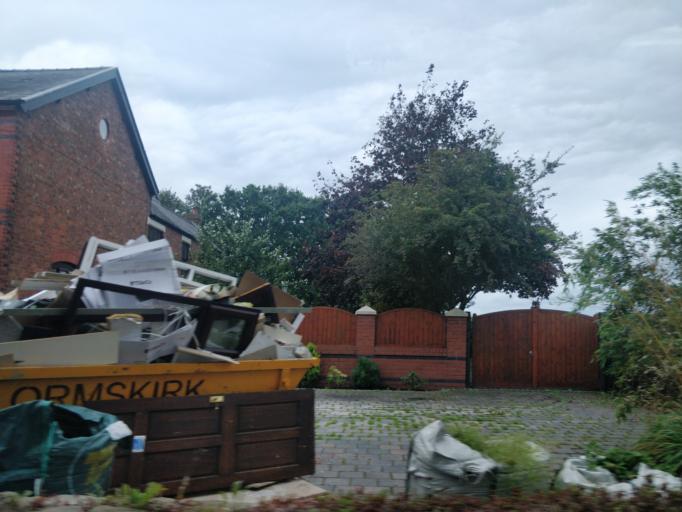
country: GB
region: England
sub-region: Lancashire
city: Ormskirk
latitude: 53.6115
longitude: -2.9172
